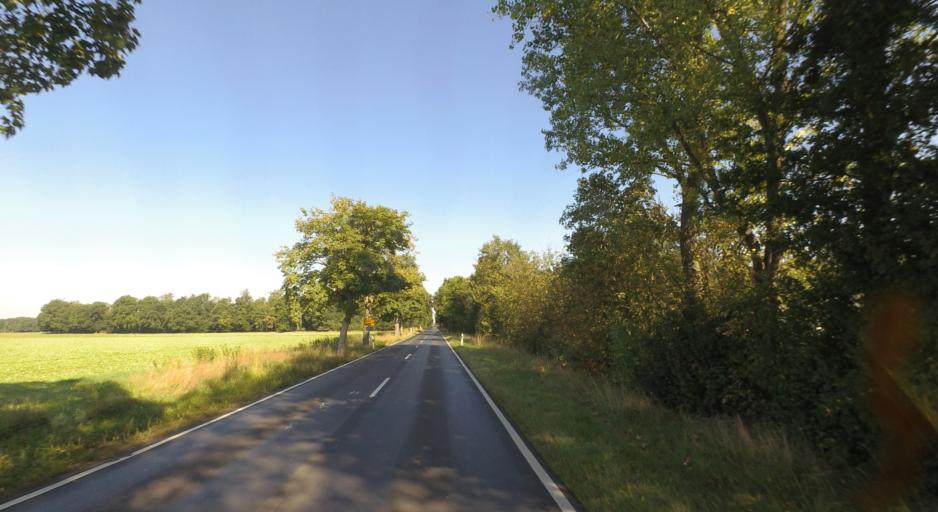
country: DE
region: Hesse
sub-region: Regierungsbezirk Darmstadt
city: Seligenstadt
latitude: 50.0235
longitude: 8.9902
